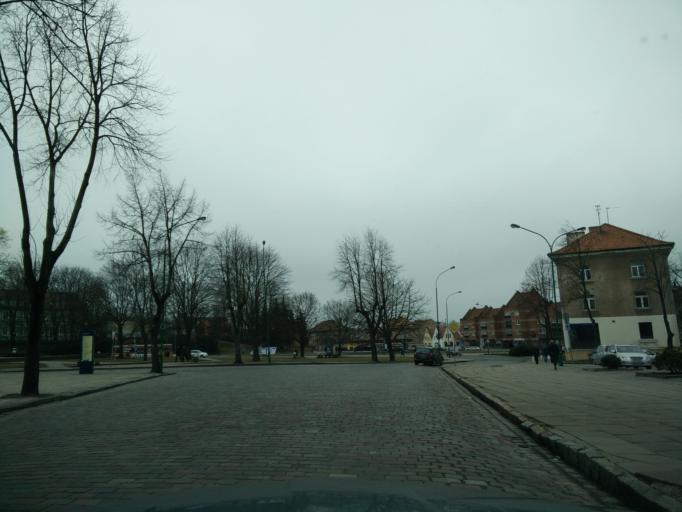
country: LT
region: Klaipedos apskritis
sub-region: Klaipeda
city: Klaipeda
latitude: 55.7074
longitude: 21.1411
